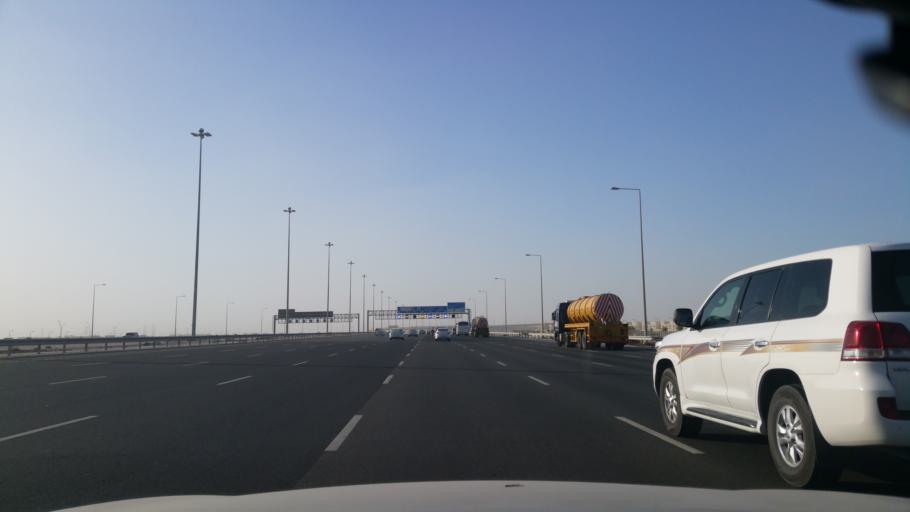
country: QA
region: Al Wakrah
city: Al Wukayr
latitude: 25.1714
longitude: 51.5585
